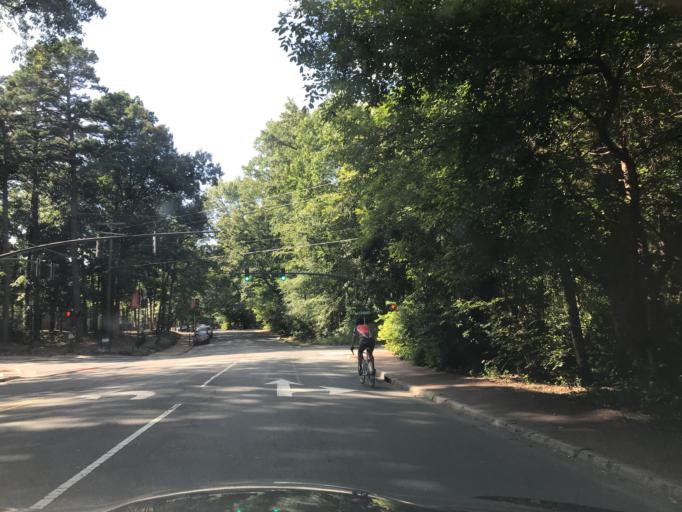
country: US
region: North Carolina
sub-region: Orange County
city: Chapel Hill
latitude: 35.9114
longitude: -79.0422
